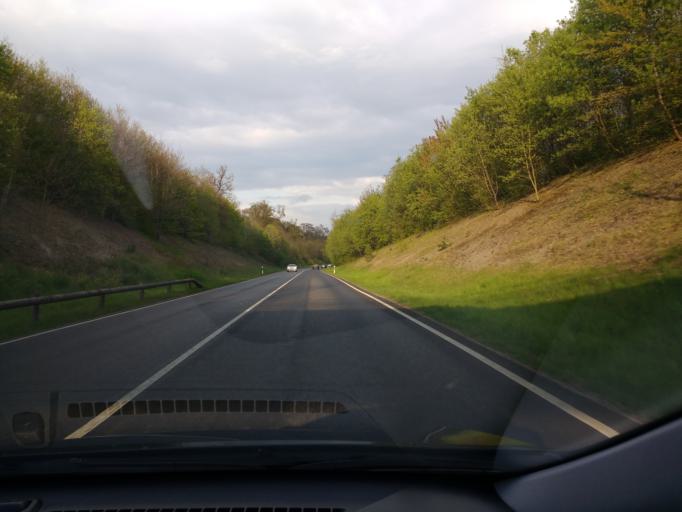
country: LU
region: Luxembourg
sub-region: Canton de Luxembourg
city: Sandweiler
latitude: 49.6095
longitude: 6.2158
